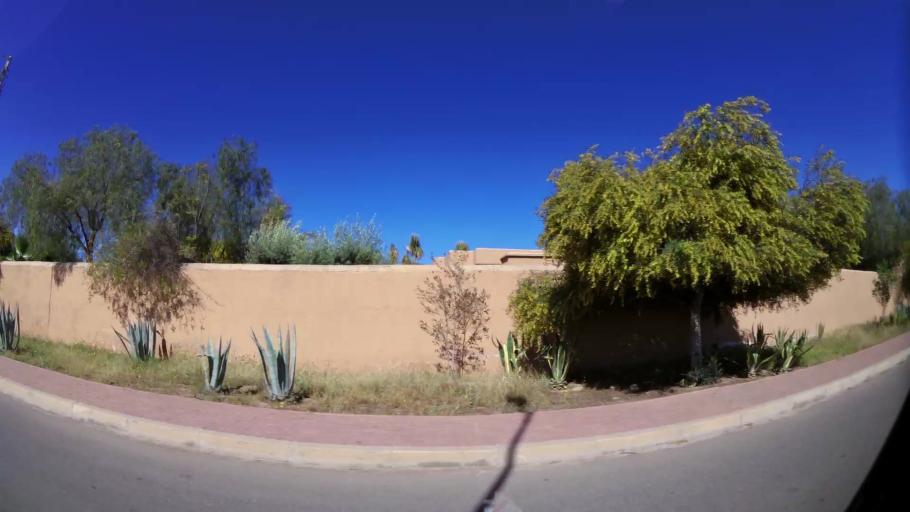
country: MA
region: Marrakech-Tensift-Al Haouz
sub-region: Marrakech
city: Marrakesh
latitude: 31.6522
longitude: -7.9356
